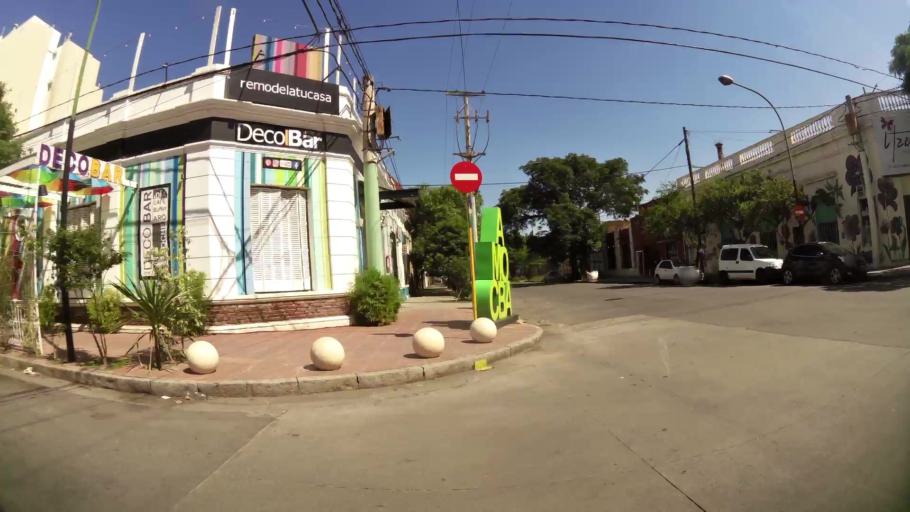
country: AR
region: Cordoba
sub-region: Departamento de Capital
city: Cordoba
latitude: -31.4175
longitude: -64.1711
